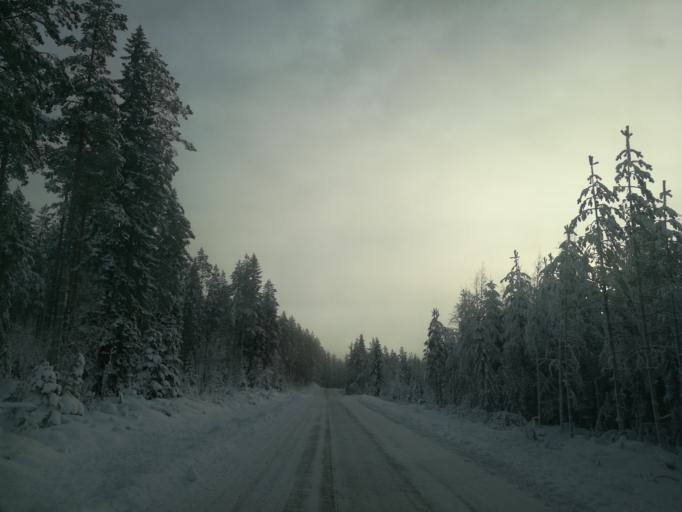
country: SE
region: Vaermland
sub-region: Torsby Kommun
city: Torsby
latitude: 60.6473
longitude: 12.7274
